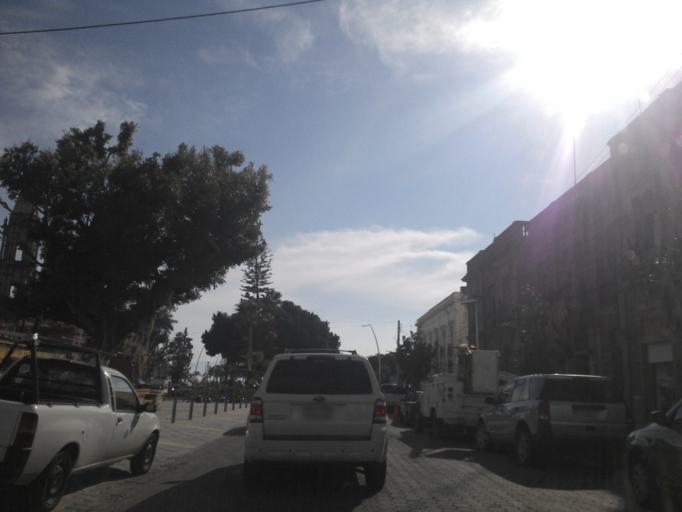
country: MX
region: Jalisco
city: Chapala
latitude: 20.2897
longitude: -103.1928
